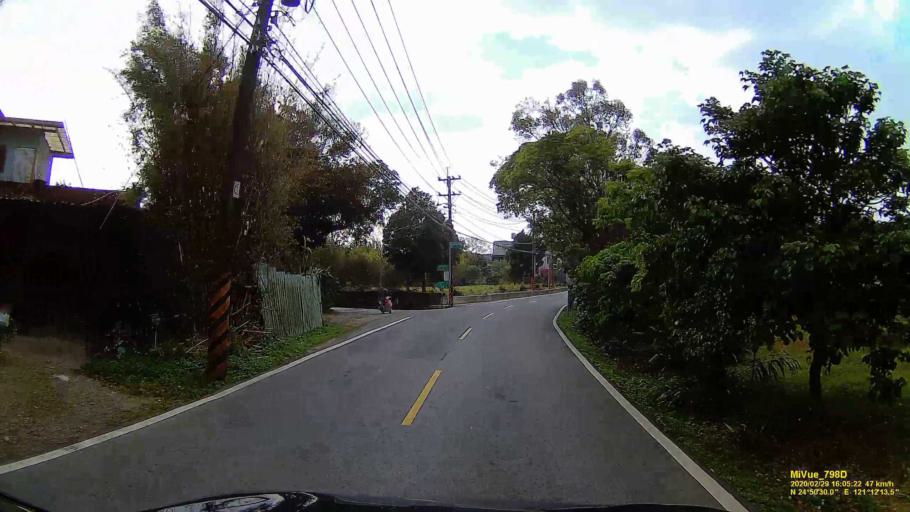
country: TW
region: Taiwan
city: Daxi
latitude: 24.8416
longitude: 121.2038
